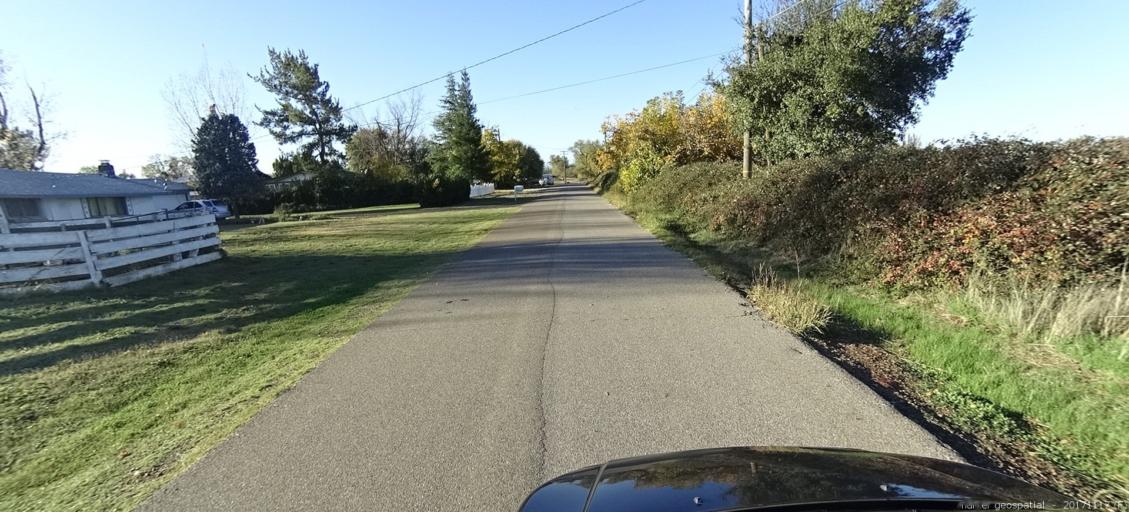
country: US
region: California
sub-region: Shasta County
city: Cottonwood
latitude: 40.4201
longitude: -122.2306
